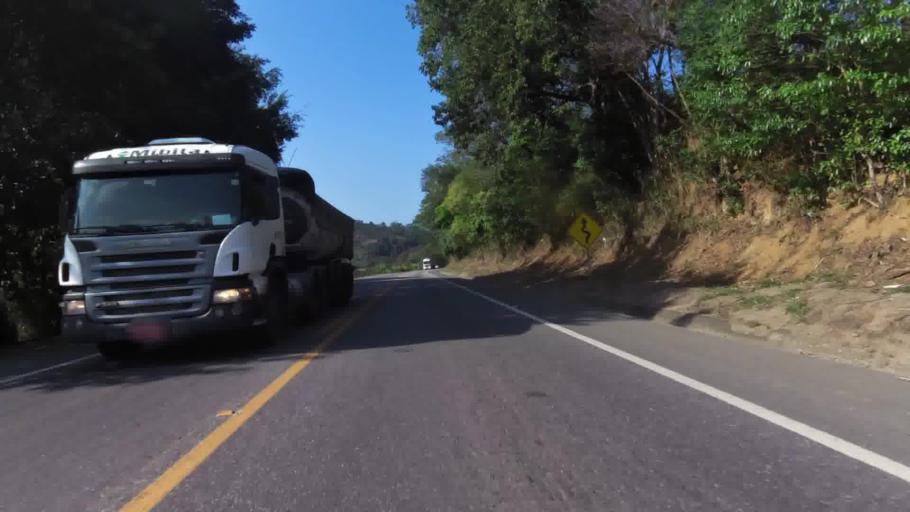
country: BR
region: Espirito Santo
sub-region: Iconha
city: Iconha
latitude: -20.8024
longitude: -40.8284
